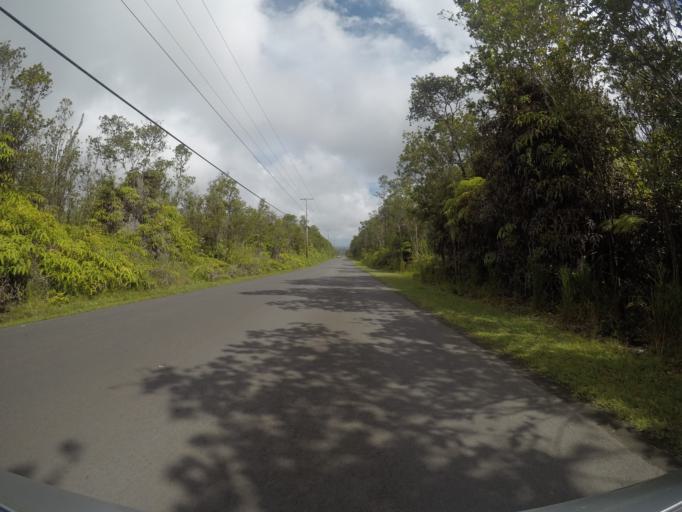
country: US
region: Hawaii
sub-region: Hawaii County
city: Fern Acres
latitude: 19.4646
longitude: -155.1337
